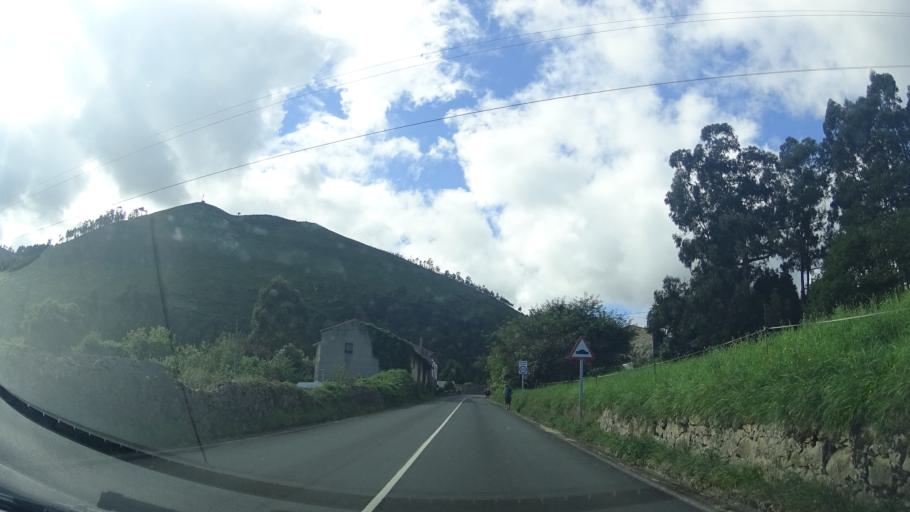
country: ES
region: Asturias
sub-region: Province of Asturias
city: Colunga
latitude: 43.4682
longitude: -5.1795
